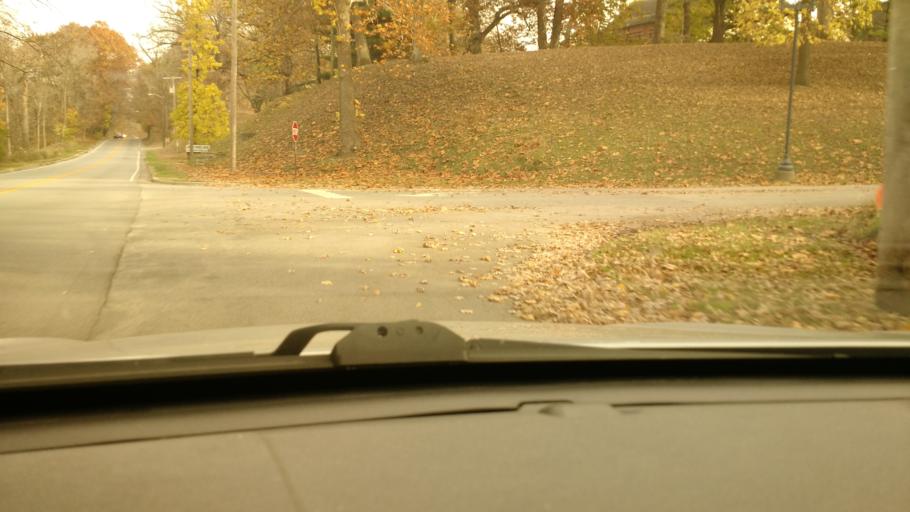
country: US
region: Illinois
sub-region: Rock Island County
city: Milan
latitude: 41.4649
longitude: -90.5740
